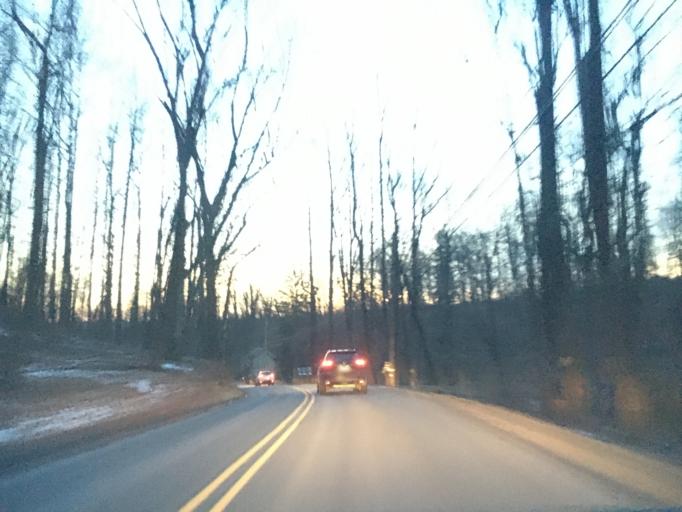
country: US
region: Pennsylvania
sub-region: Northampton County
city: Cherryville
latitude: 40.7419
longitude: -75.5424
